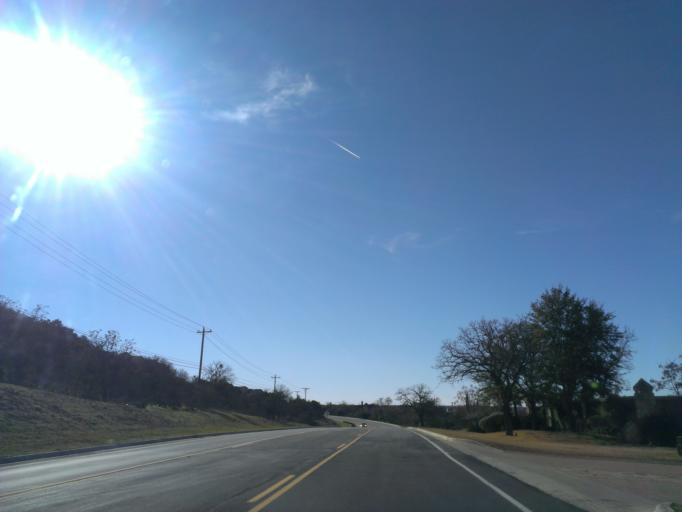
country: US
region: Texas
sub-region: Llano County
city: Horseshoe Bay
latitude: 30.5491
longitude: -98.3422
